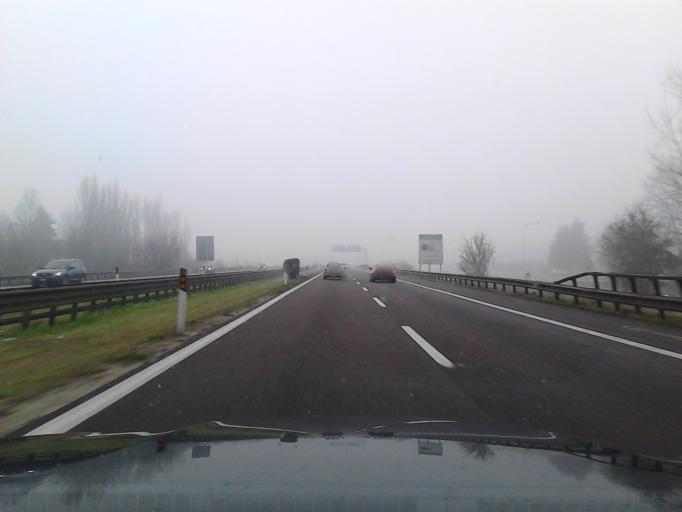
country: IT
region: Emilia-Romagna
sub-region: Provincia di Modena
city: Campogalliano
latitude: 44.6838
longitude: 10.8494
